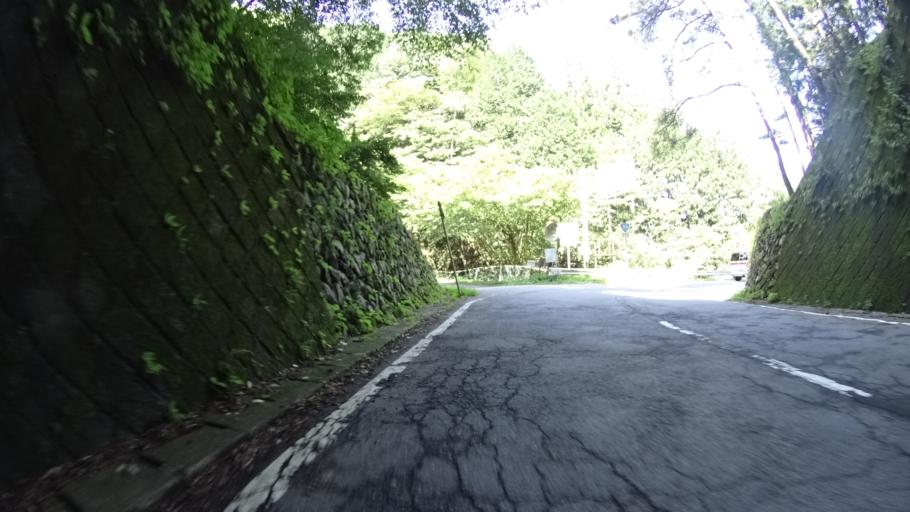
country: JP
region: Gunma
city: Tomioka
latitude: 36.0591
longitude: 138.8434
